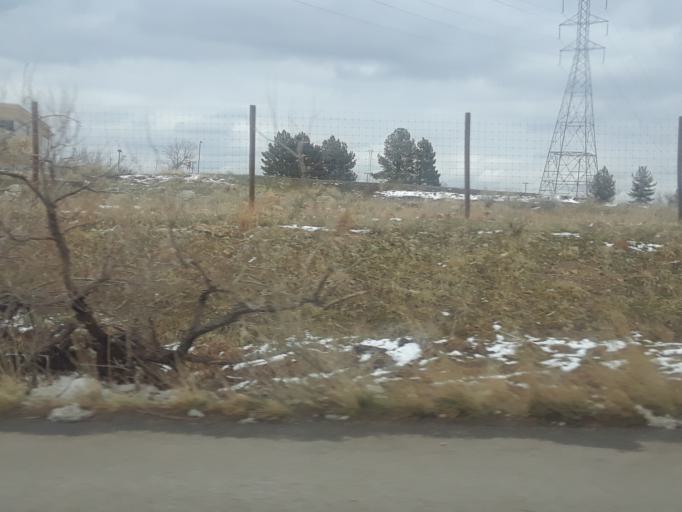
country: US
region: Colorado
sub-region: Jefferson County
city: Golden
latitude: 39.7322
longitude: -105.2120
